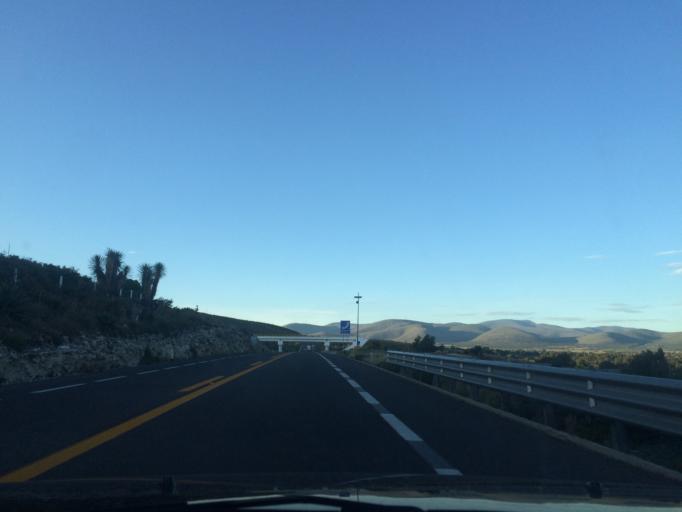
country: MX
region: Puebla
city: Cuacnopalan
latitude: 18.7969
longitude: -97.4895
